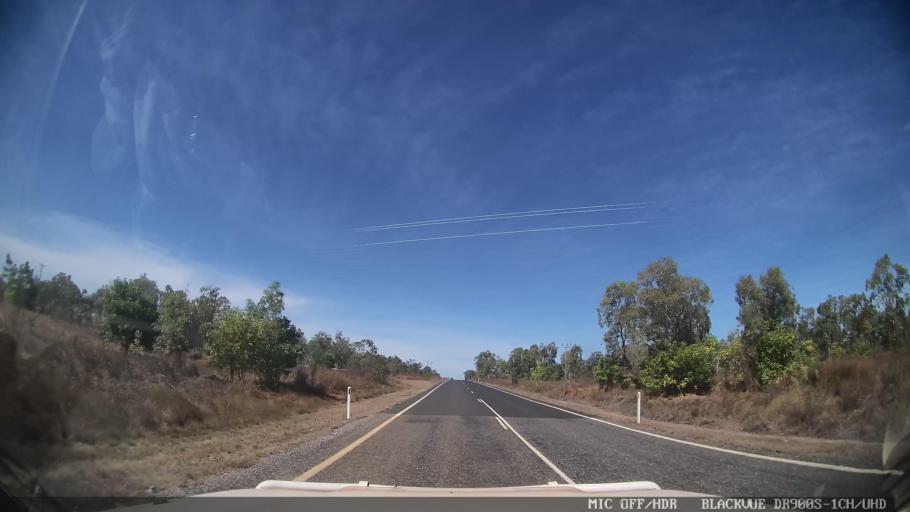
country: AU
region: Queensland
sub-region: Cook
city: Cooktown
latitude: -15.8657
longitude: 144.8086
